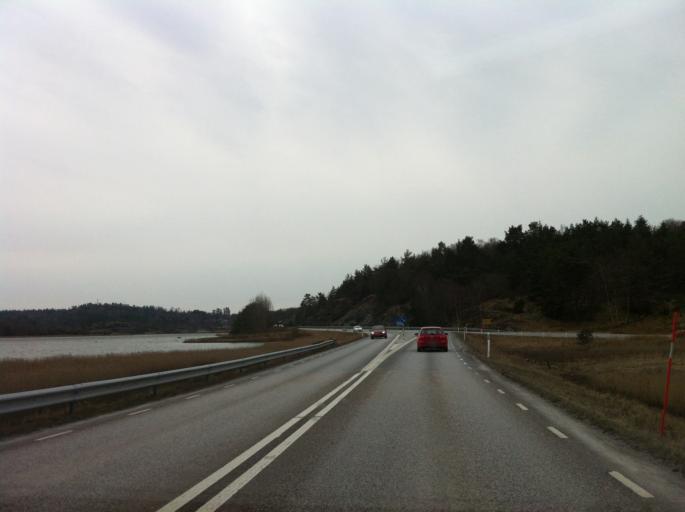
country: SE
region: Vaestra Goetaland
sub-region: Orust
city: Henan
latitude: 58.2756
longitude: 11.6939
